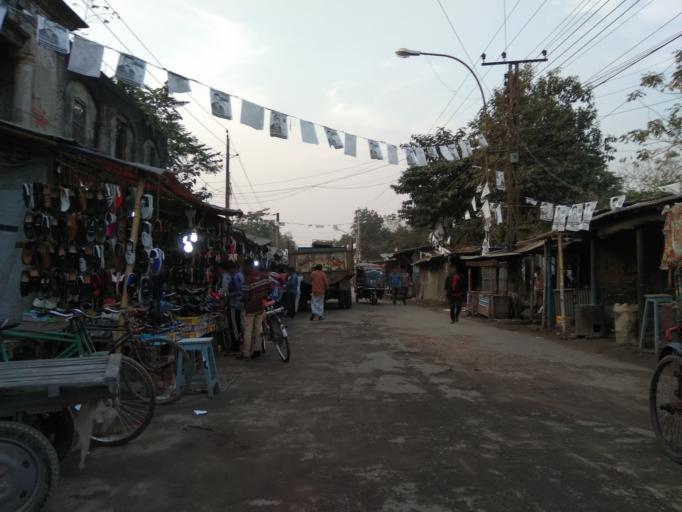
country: BD
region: Rangpur Division
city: Rangpur
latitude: 25.7294
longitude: 89.2636
